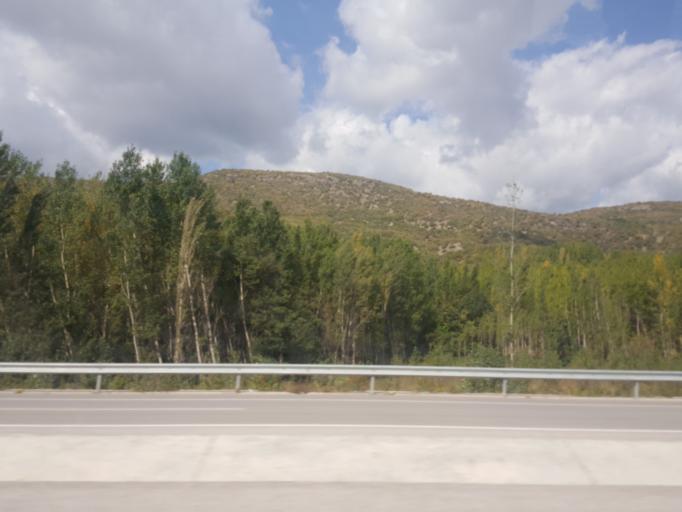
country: TR
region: Tokat
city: Gokdere
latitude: 40.3965
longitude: 36.7046
